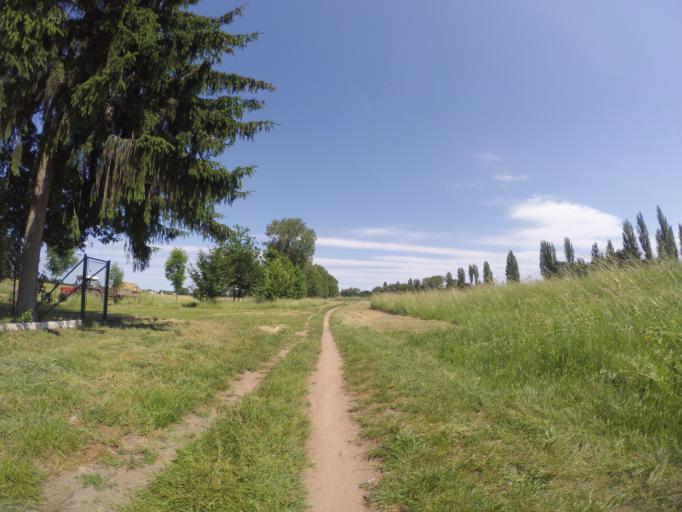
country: CZ
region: Central Bohemia
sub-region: Okres Nymburk
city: Sadska
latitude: 50.1705
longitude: 14.9899
